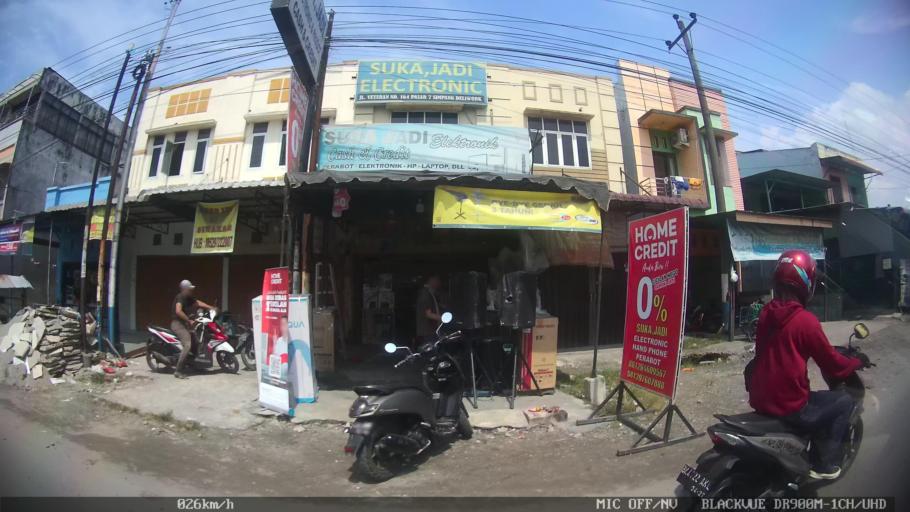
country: ID
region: North Sumatra
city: Medan
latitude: 3.6525
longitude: 98.6570
